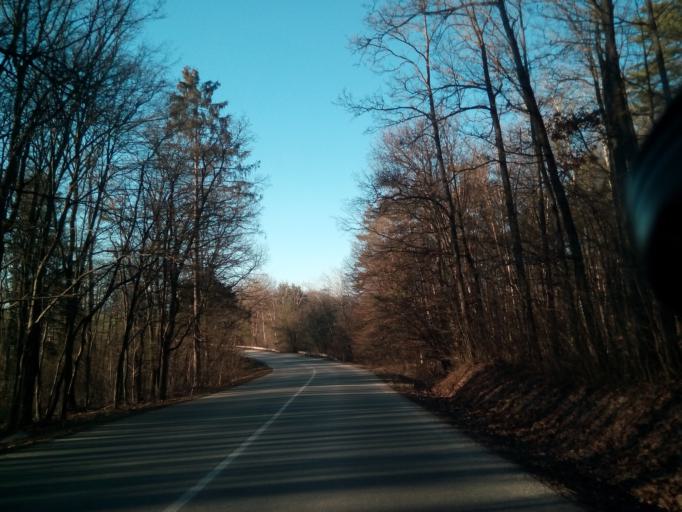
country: SK
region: Kosicky
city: Moldava nad Bodvou
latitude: 48.6904
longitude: 21.0296
